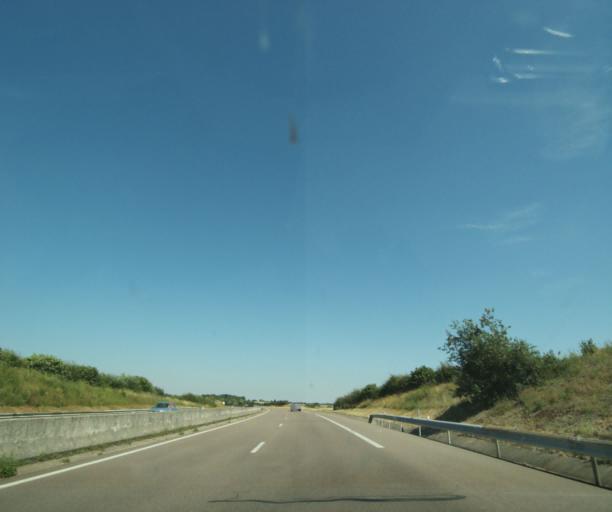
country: FR
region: Lorraine
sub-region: Departement des Vosges
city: Chatenois
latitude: 48.4029
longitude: 5.8794
